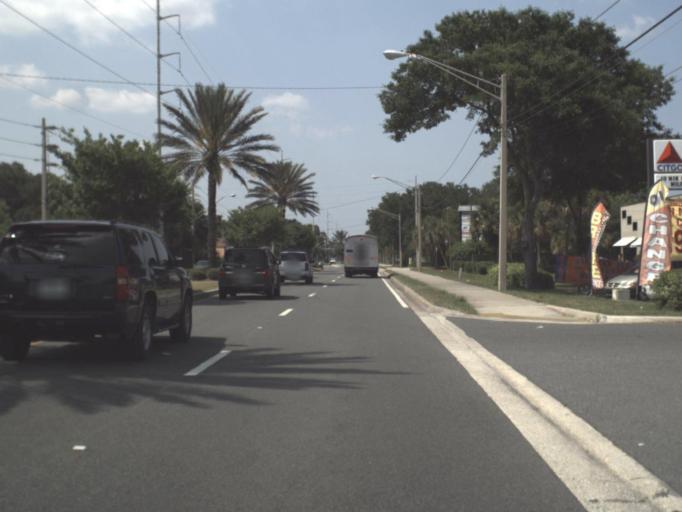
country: US
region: Florida
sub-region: Duval County
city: Atlantic Beach
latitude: 30.3579
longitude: -81.4130
